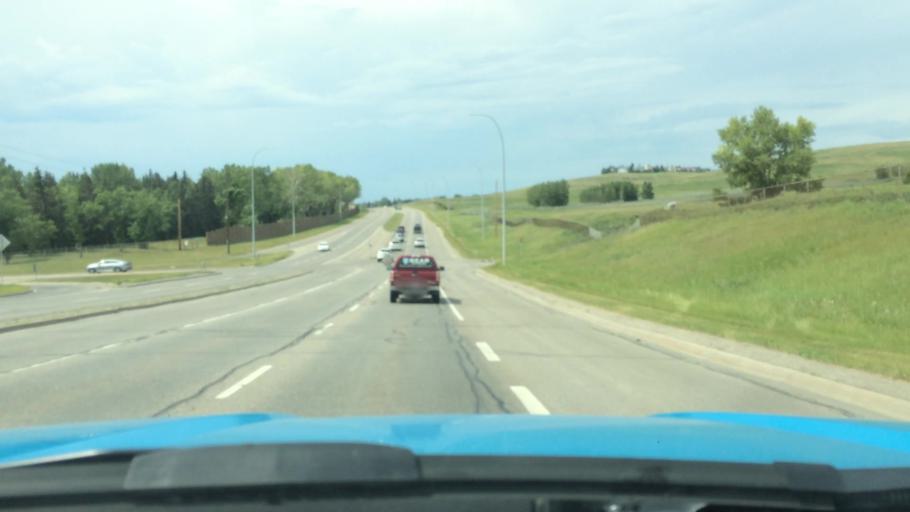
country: CA
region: Alberta
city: Calgary
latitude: 51.1027
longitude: -114.1262
